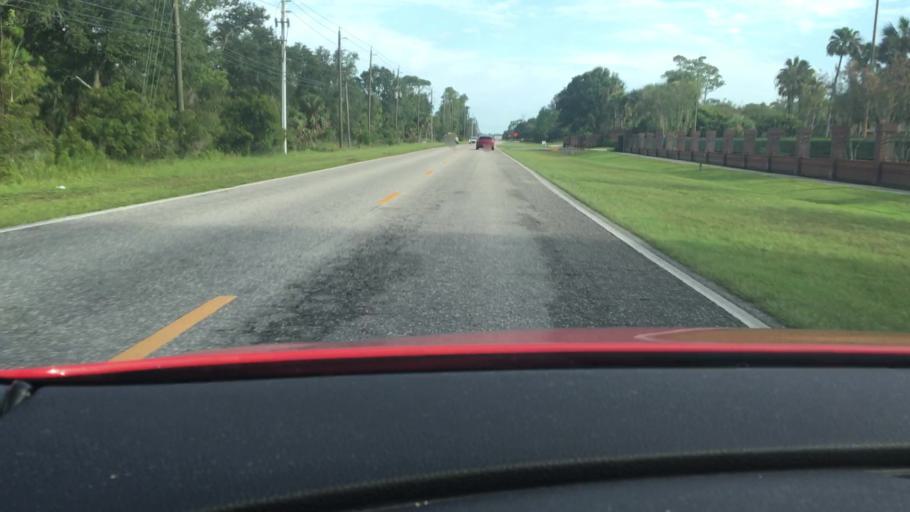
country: US
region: Florida
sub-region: Volusia County
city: Daytona Beach
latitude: 29.1746
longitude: -81.0898
